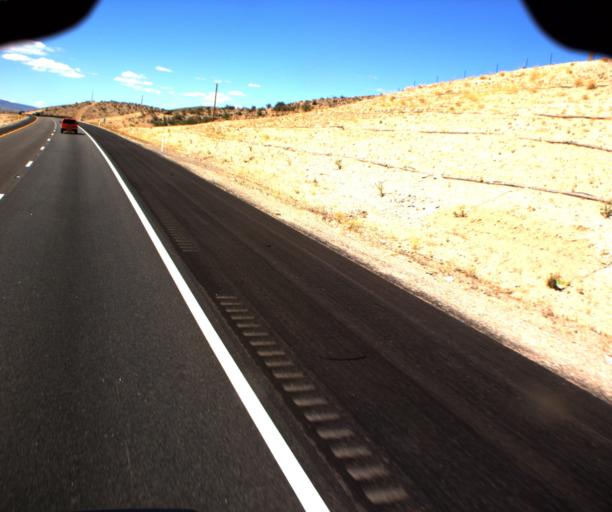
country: US
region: Arizona
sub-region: Mohave County
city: Kingman
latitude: 34.9971
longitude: -113.6641
